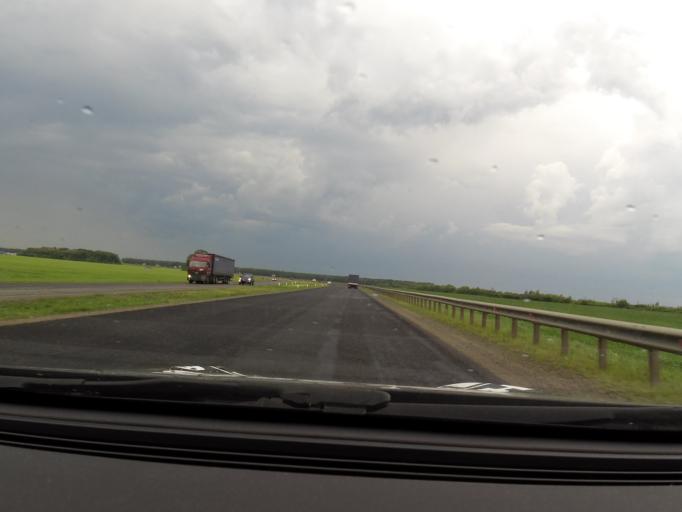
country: RU
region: Bashkortostan
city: Asanovo
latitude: 54.9772
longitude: 55.5693
